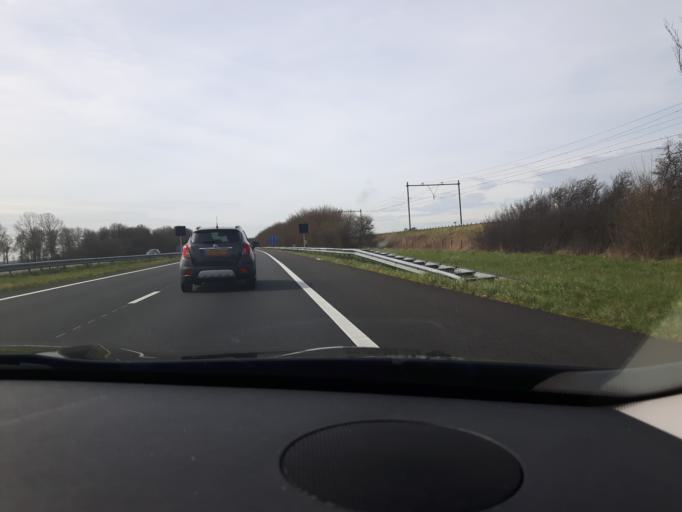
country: NL
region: Zeeland
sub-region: Gemeente Noord-Beveland
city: Kamperland
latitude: 51.5025
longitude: 3.7239
